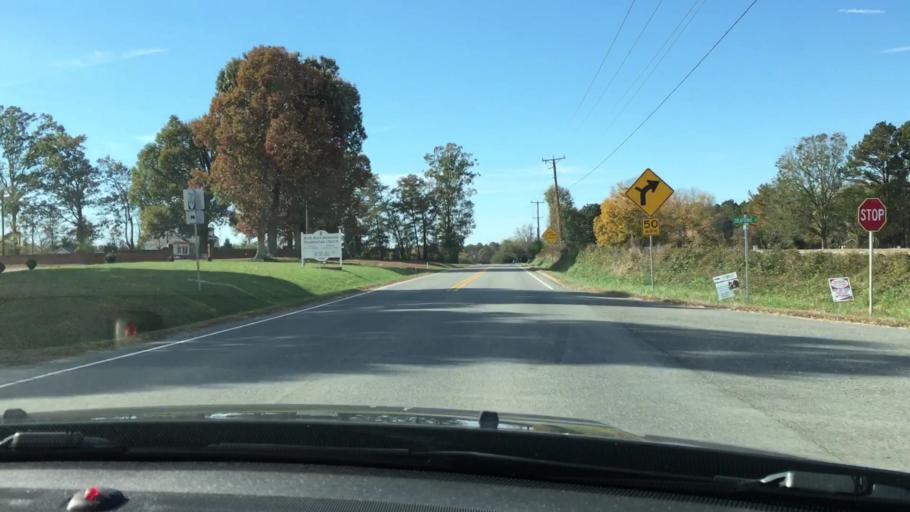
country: US
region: Virginia
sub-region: King and Queen County
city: King and Queen Court House
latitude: 37.5915
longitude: -76.8933
